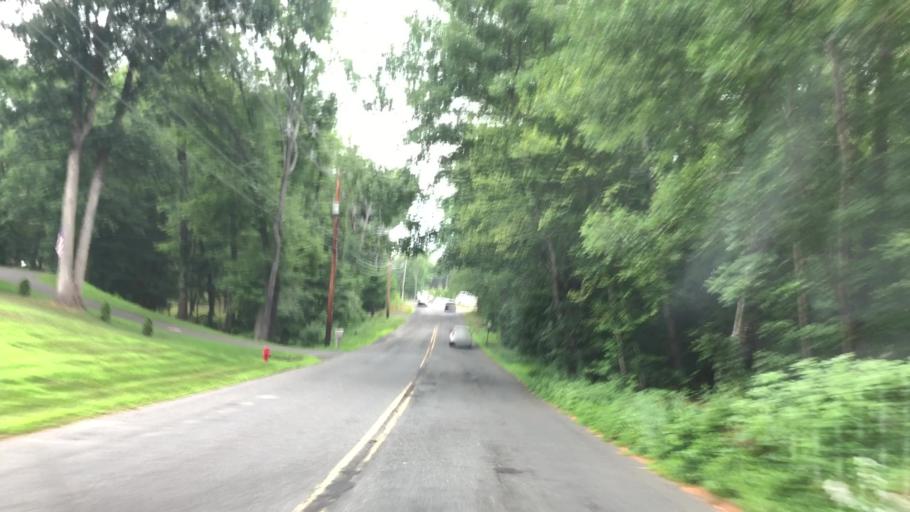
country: US
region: Massachusetts
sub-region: Hampden County
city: Westfield
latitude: 42.1732
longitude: -72.7483
